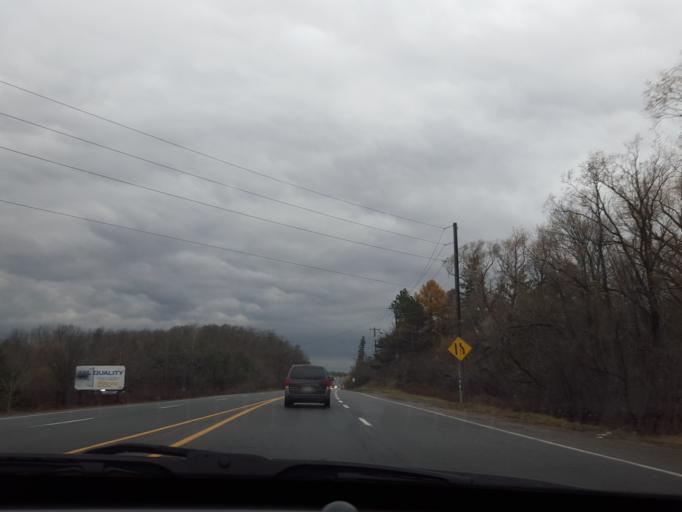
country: CA
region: Ontario
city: Pickering
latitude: 43.8894
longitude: -79.0920
